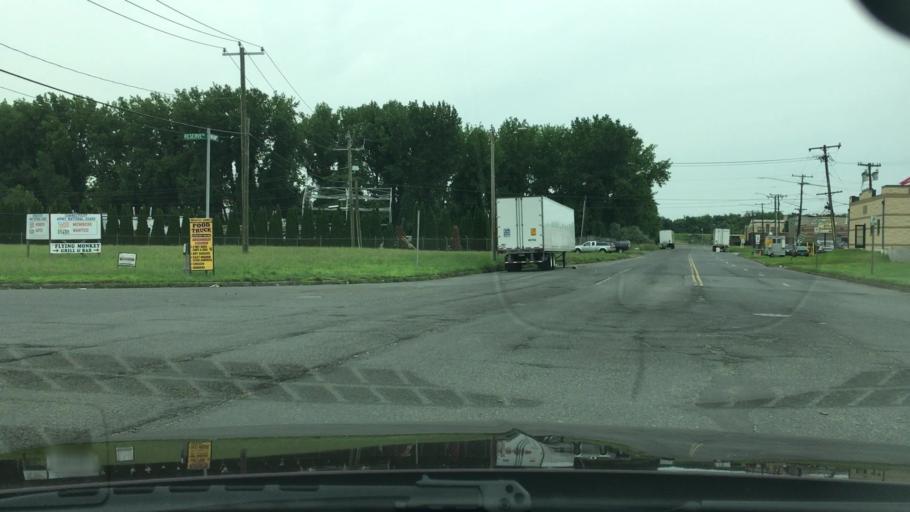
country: US
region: Connecticut
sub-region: Hartford County
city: Wethersfield
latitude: 41.7445
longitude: -72.6544
